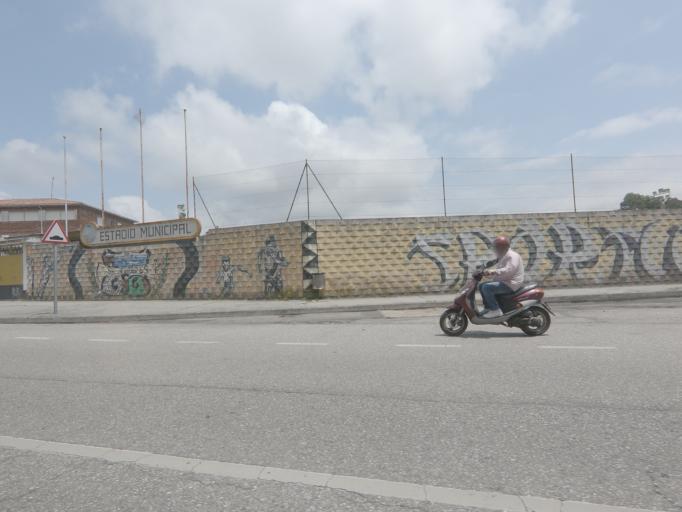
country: ES
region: Galicia
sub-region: Provincia de Pontevedra
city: A Guarda
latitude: 41.8993
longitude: -8.8622
